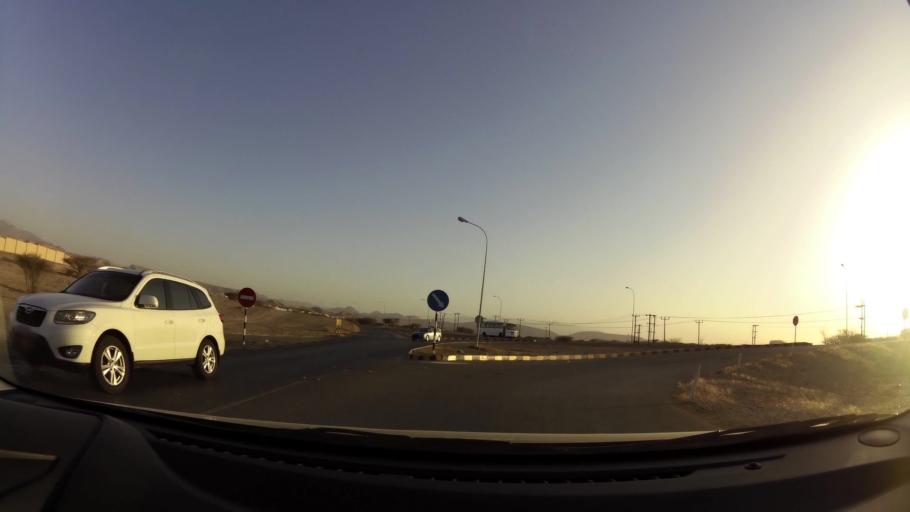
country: OM
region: Muhafazat Masqat
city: As Sib al Jadidah
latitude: 23.5884
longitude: 58.2147
